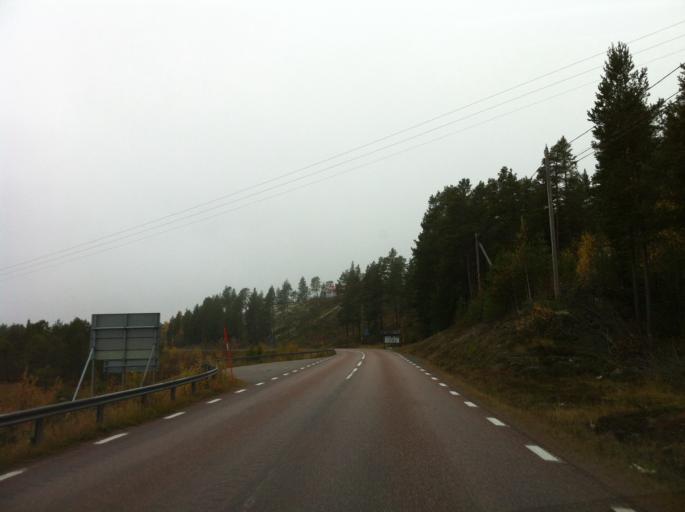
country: NO
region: Hedmark
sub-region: Trysil
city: Innbygda
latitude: 61.8545
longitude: 12.7410
